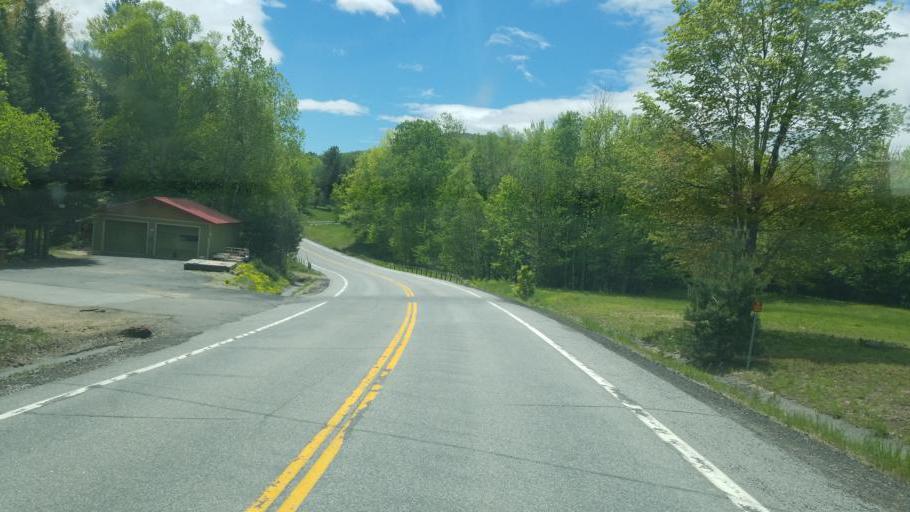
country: US
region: New York
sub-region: Hamilton County
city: Lake Pleasant
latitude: 43.7481
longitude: -74.2898
